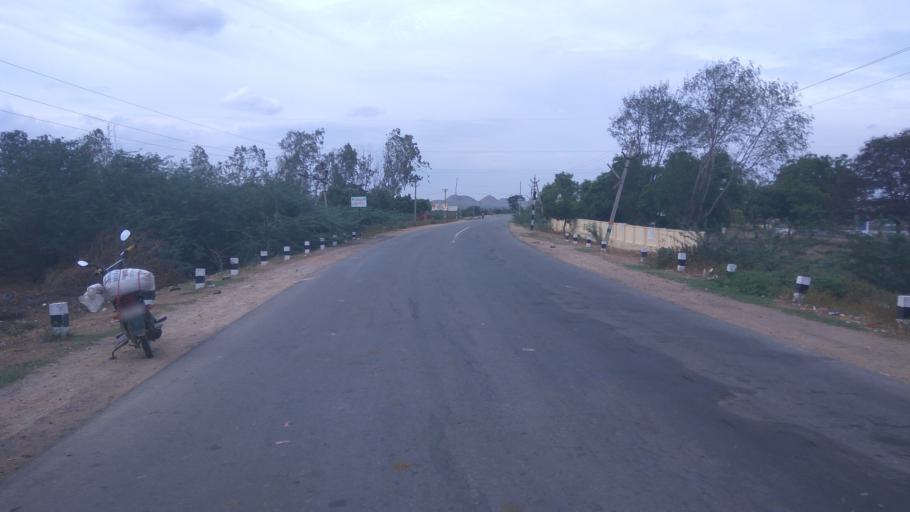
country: IN
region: Andhra Pradesh
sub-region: Prakasam
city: Cumbum
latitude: 15.5936
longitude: 79.1162
